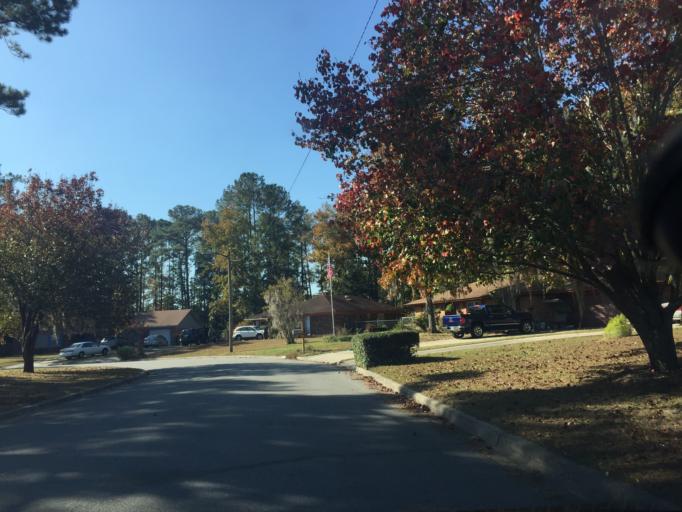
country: US
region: Georgia
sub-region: Chatham County
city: Montgomery
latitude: 31.9951
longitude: -81.1403
